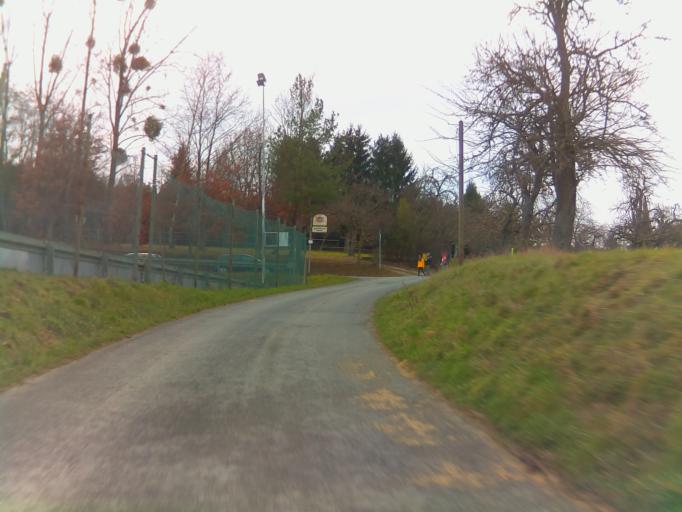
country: DE
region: Bavaria
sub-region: Regierungsbezirk Unterfranken
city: Hausen
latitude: 49.8765
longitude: 9.2051
